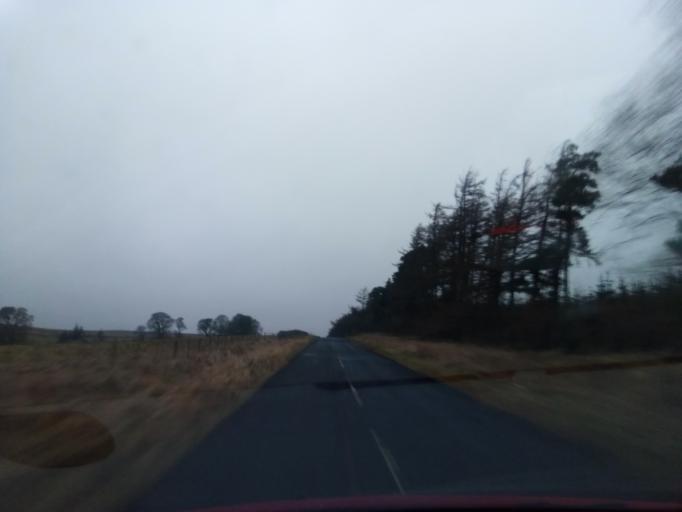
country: GB
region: England
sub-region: Northumberland
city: Otterburn
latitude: 55.2086
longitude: -2.0407
